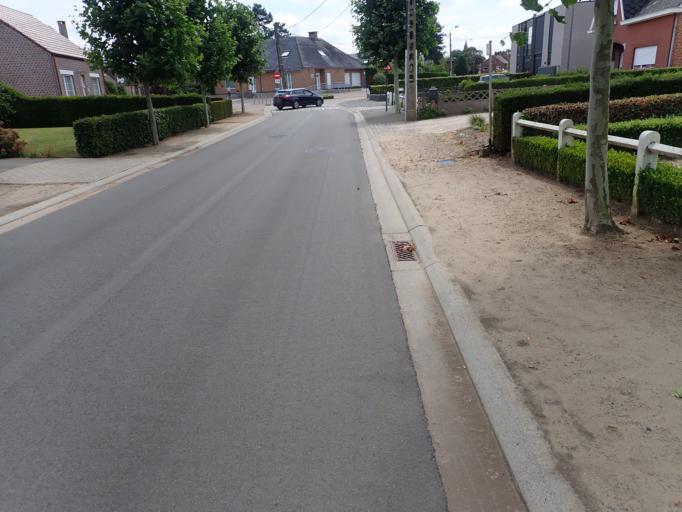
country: BE
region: Flanders
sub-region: Provincie Vlaams-Brabant
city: Keerbergen
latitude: 51.0078
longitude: 4.6301
